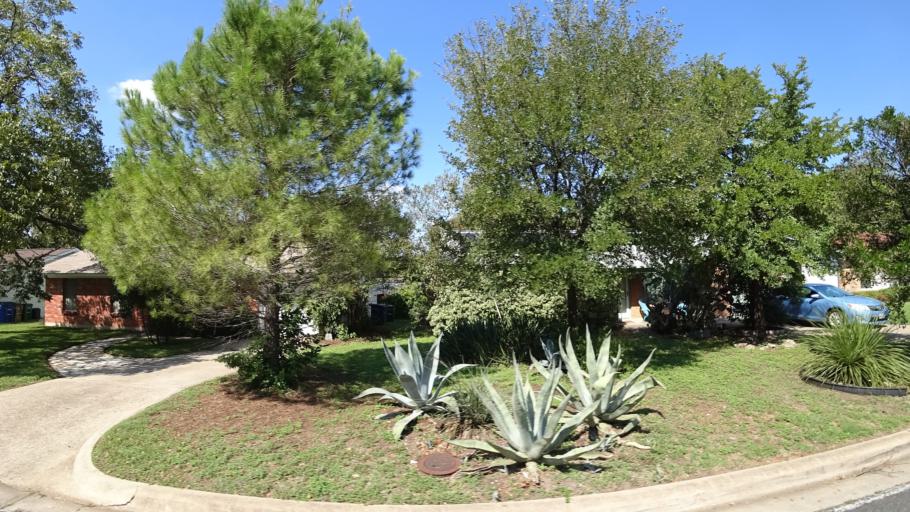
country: US
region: Texas
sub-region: Travis County
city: Austin
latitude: 30.3344
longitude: -97.7120
